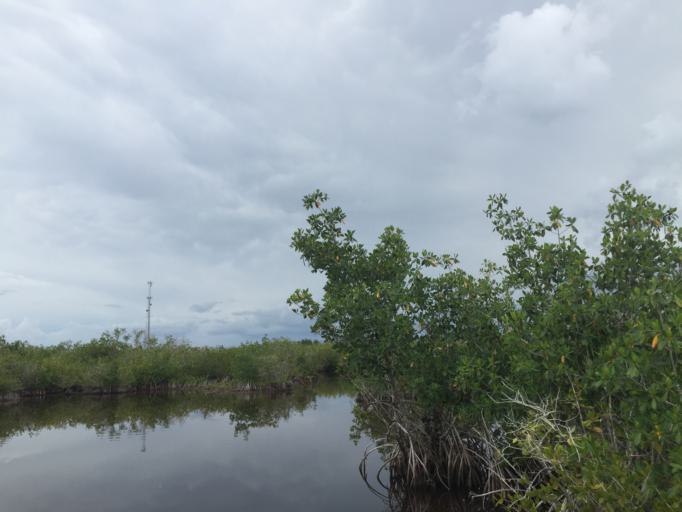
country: US
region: Florida
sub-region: Collier County
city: Marco
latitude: 25.9085
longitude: -81.3678
